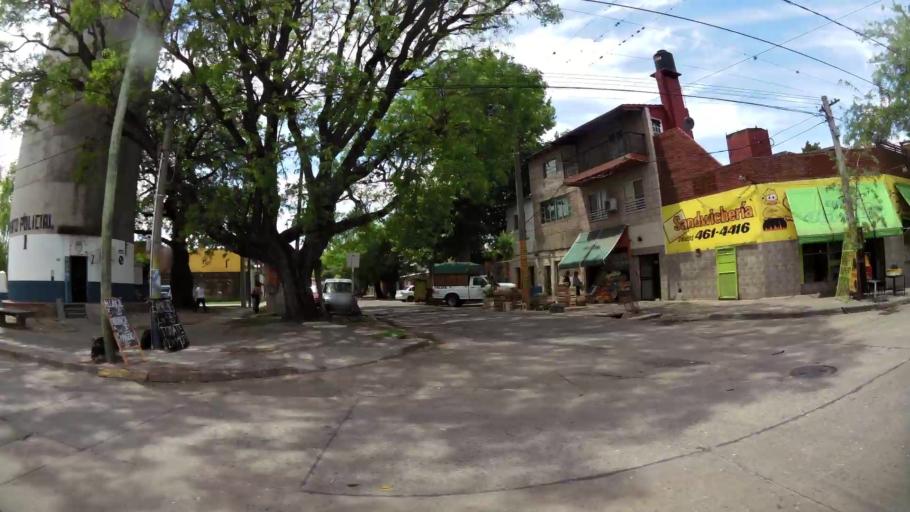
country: AR
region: Santa Fe
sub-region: Departamento de Rosario
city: Rosario
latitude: -32.9867
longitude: -60.6283
